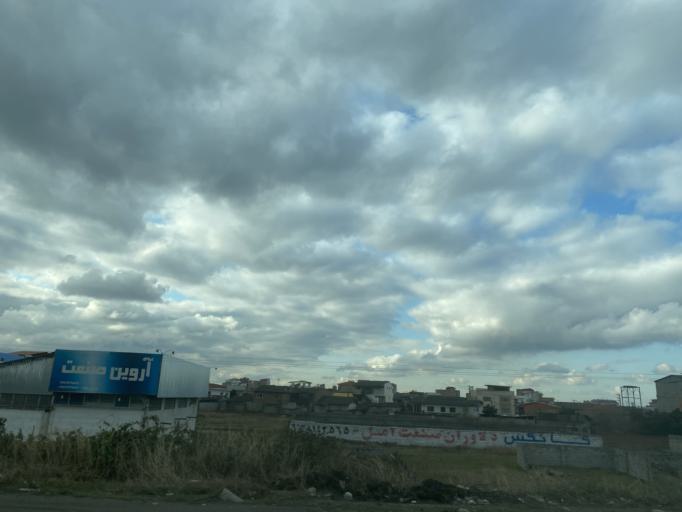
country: IR
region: Mazandaran
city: Amol
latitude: 36.4500
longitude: 52.3937
